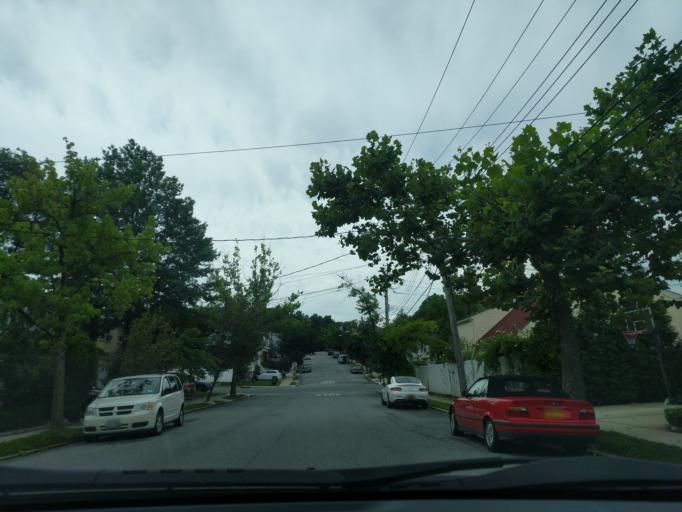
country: US
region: New York
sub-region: Richmond County
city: Staten Island
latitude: 40.6023
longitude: -74.1225
